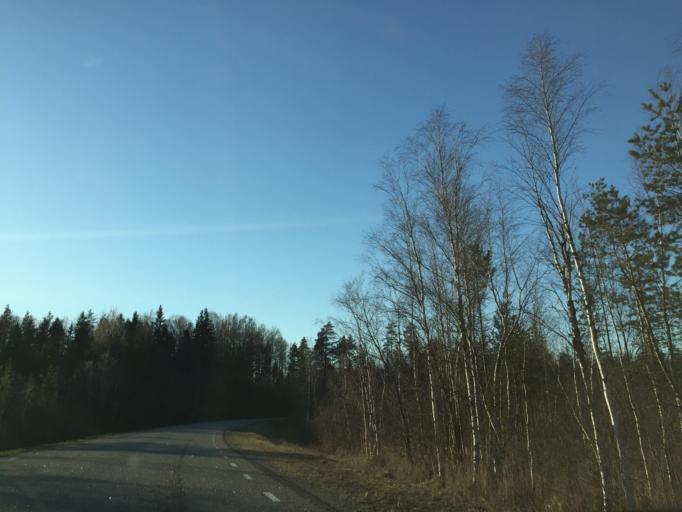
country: EE
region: Ida-Virumaa
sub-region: Toila vald
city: Voka
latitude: 59.1281
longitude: 27.6144
